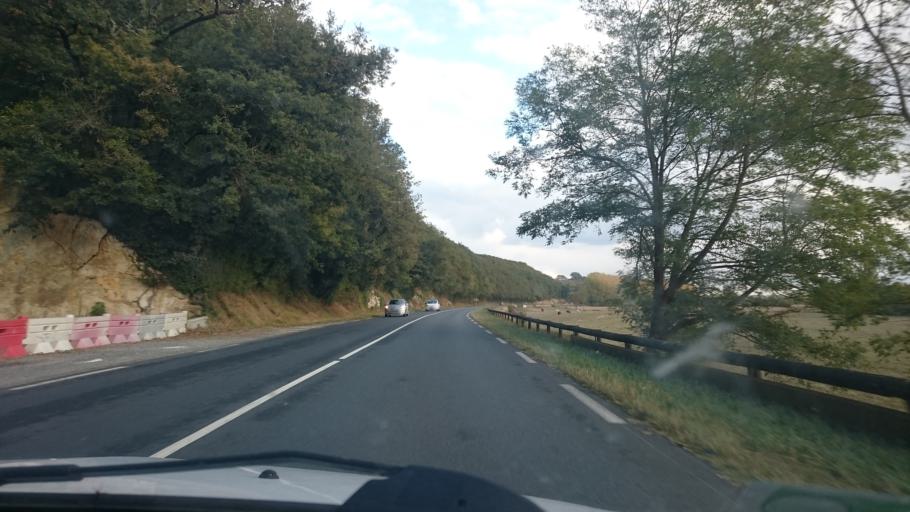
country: FR
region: Centre
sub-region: Departement de l'Indre
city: Saint-Gaultier
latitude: 46.6376
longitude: 1.4437
